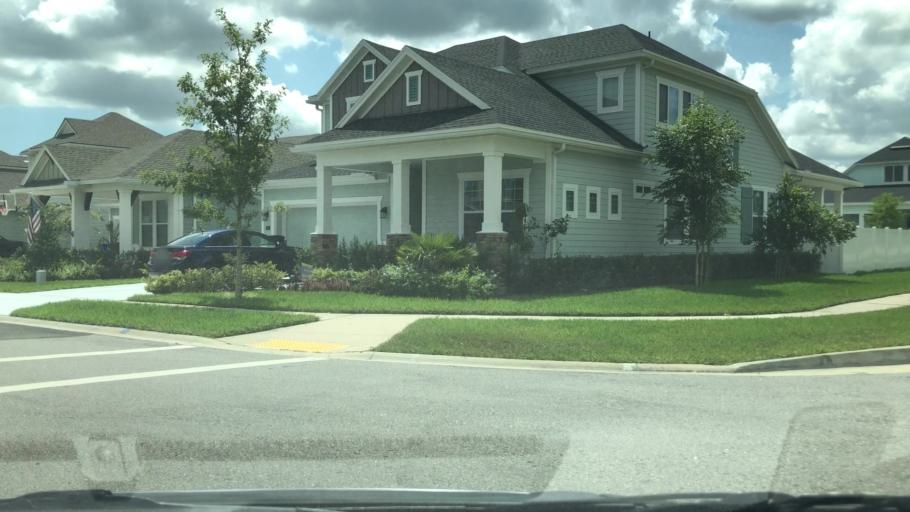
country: US
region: Florida
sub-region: Saint Johns County
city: Palm Valley
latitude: 30.1119
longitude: -81.4270
